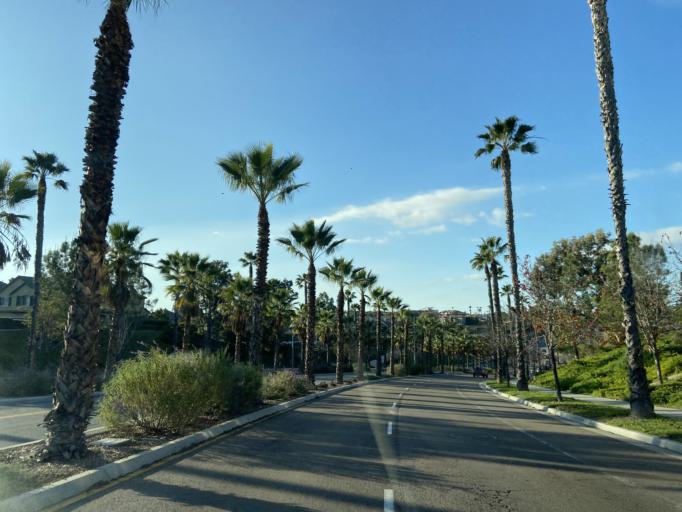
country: US
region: California
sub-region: San Diego County
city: Bonita
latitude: 32.6276
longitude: -116.9771
